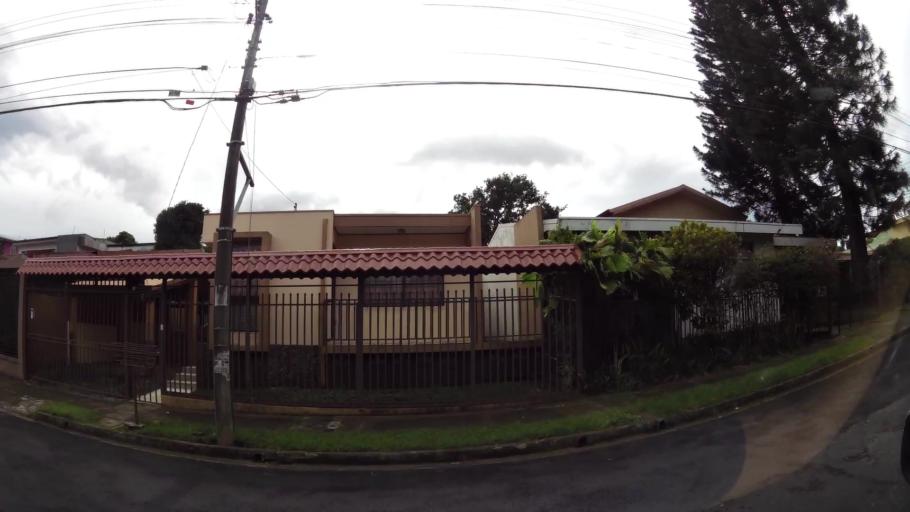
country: CR
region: San Jose
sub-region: Canton de Goicoechea
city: Guadalupe
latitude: 9.9584
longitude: -84.0591
